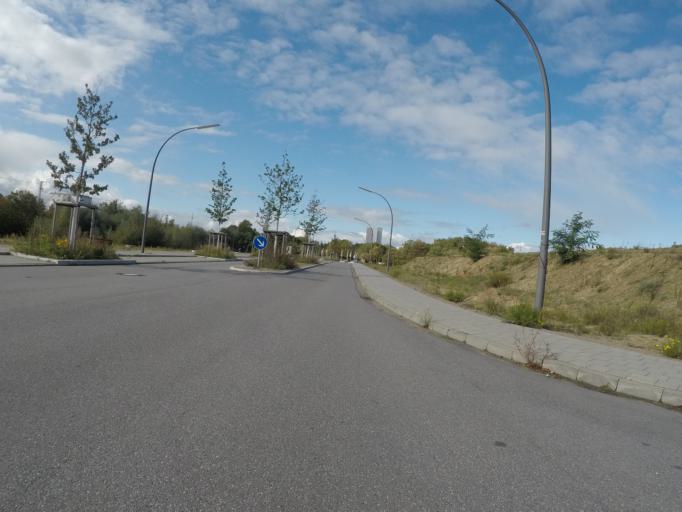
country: DE
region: Hamburg
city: Rothenburgsort
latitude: 53.5395
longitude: 10.0366
